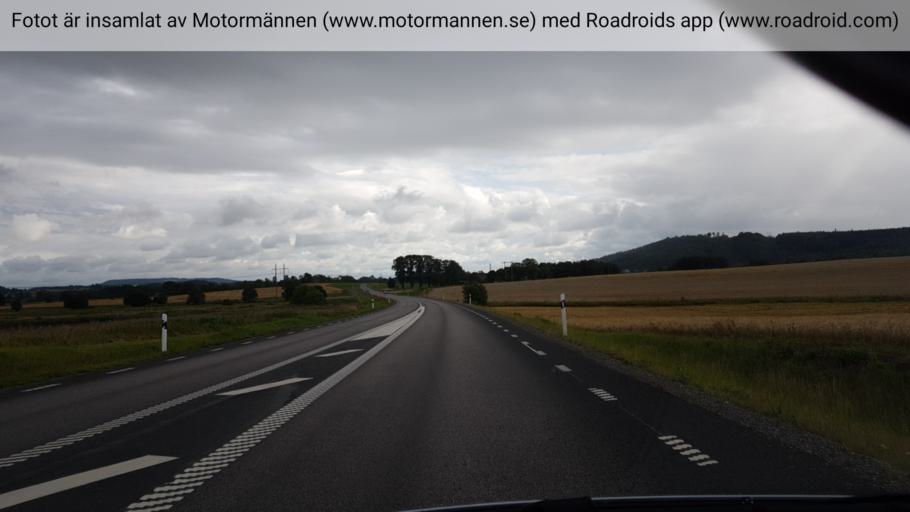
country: SE
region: Vaestra Goetaland
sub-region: Falkopings Kommun
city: Falkoeping
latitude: 58.2078
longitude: 13.5609
